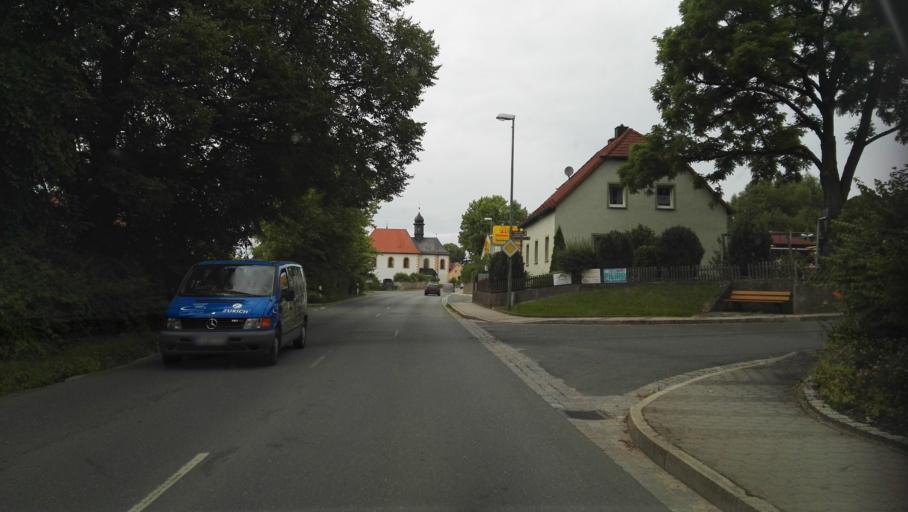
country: DE
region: Bavaria
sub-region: Upper Franconia
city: Hollfeld
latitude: 49.9331
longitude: 11.2957
